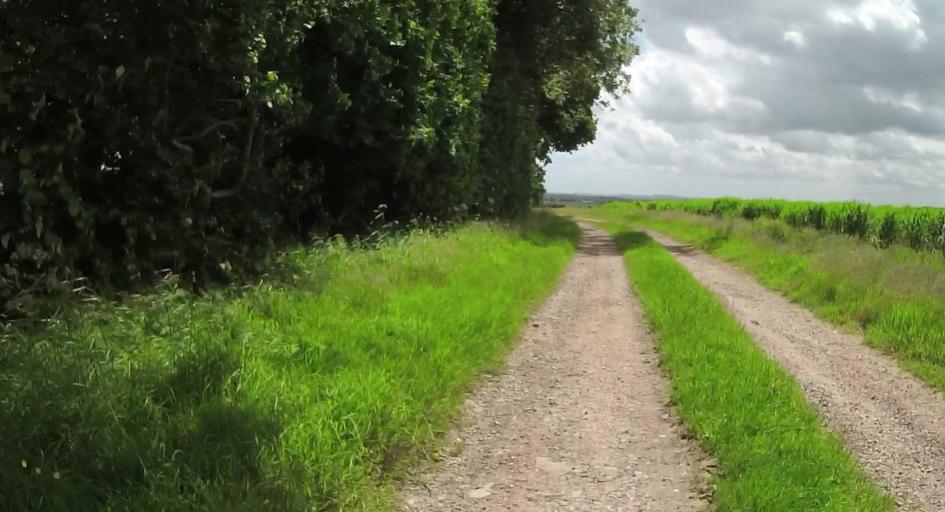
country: GB
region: England
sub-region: Hampshire
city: Basingstoke
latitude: 51.1799
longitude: -1.1647
